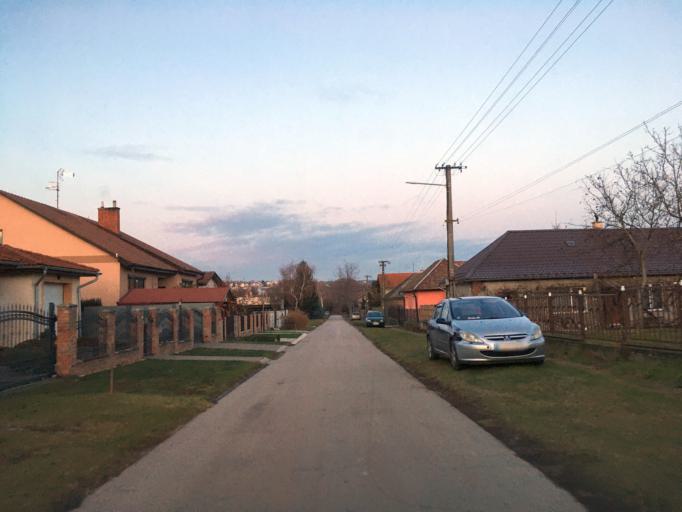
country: SK
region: Nitriansky
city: Svodin
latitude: 47.8956
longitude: 18.4170
